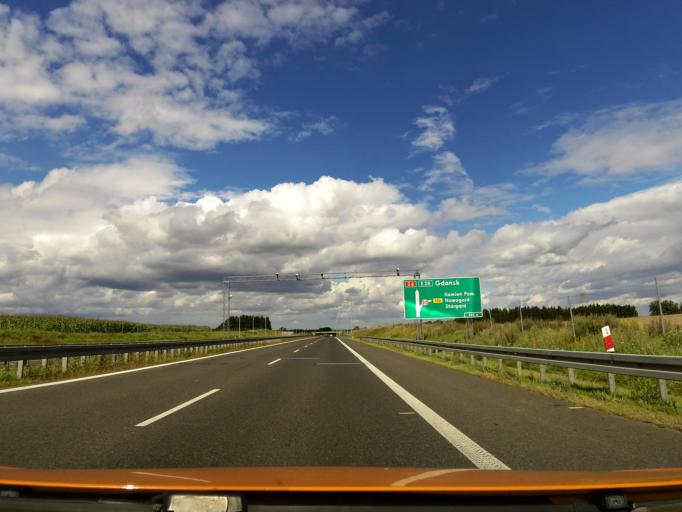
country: PL
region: West Pomeranian Voivodeship
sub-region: Powiat goleniowski
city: Nowogard
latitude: 53.6792
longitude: 15.0845
